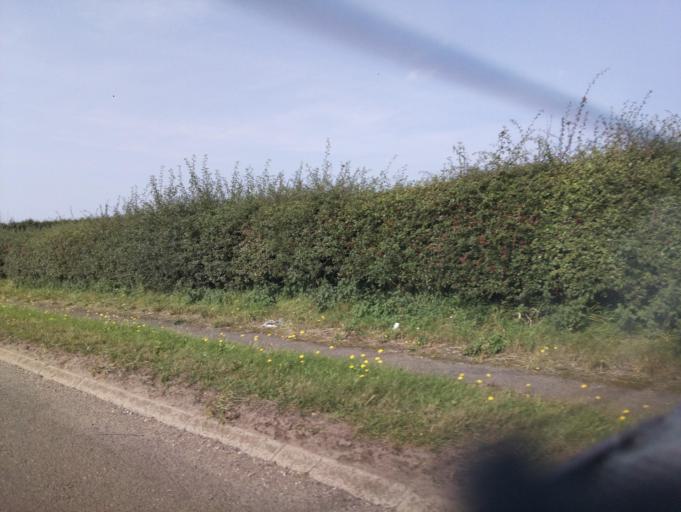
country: GB
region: England
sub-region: Walsall
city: Brownhills
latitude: 52.6460
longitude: -1.8994
